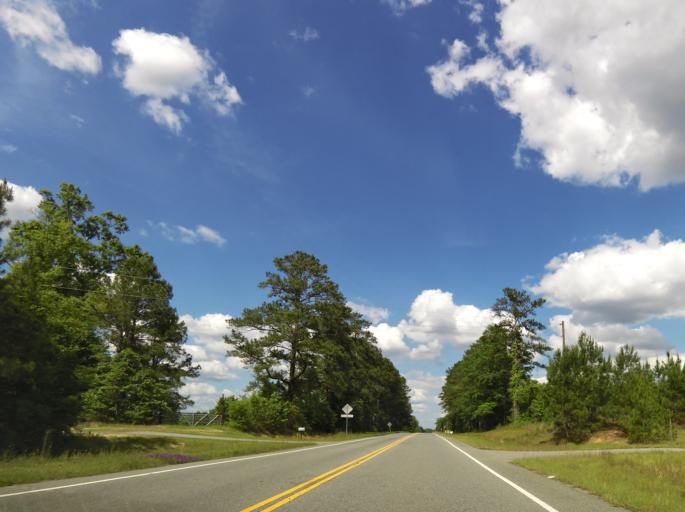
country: US
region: Georgia
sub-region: Treutlen County
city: Soperton
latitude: 32.3130
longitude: -82.6875
